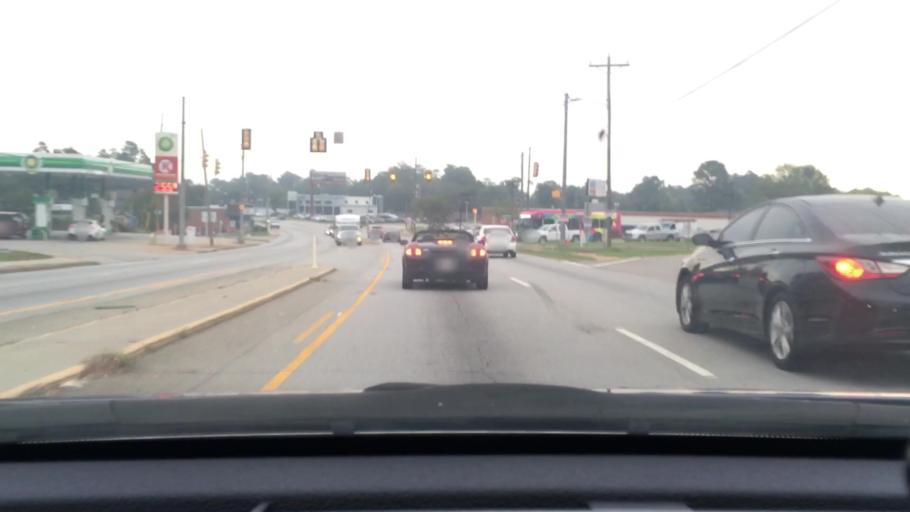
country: US
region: South Carolina
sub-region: Lexington County
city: West Columbia
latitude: 34.0251
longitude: -81.0796
